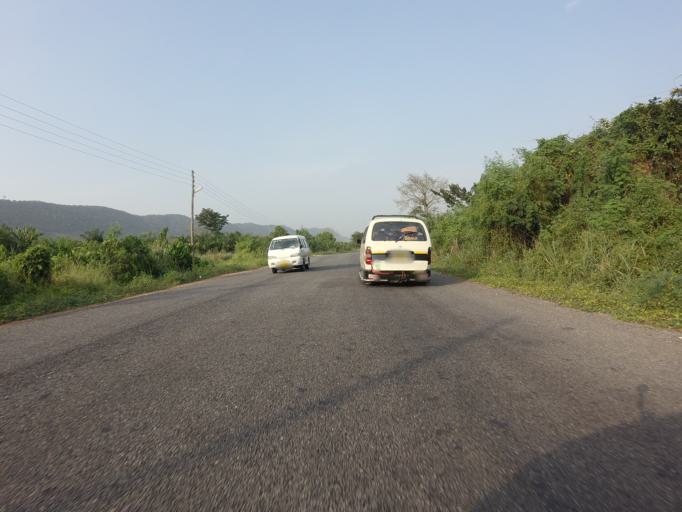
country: GH
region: Volta
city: Ho
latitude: 6.4346
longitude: 0.1918
